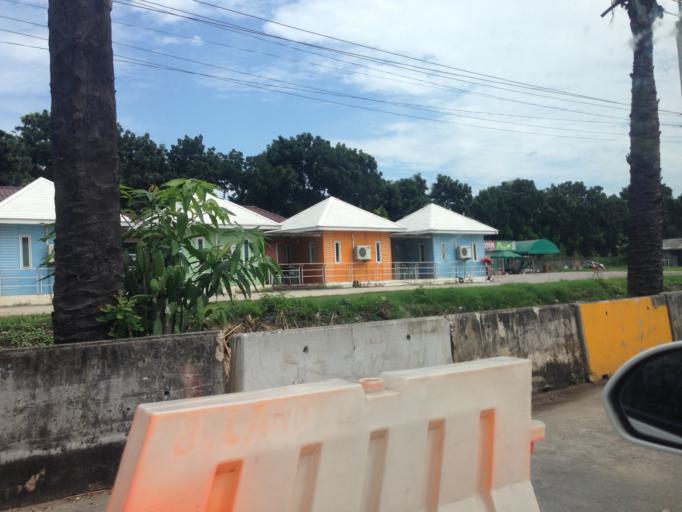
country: TH
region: Nonthaburi
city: Pak Kret
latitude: 13.9347
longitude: 100.5368
